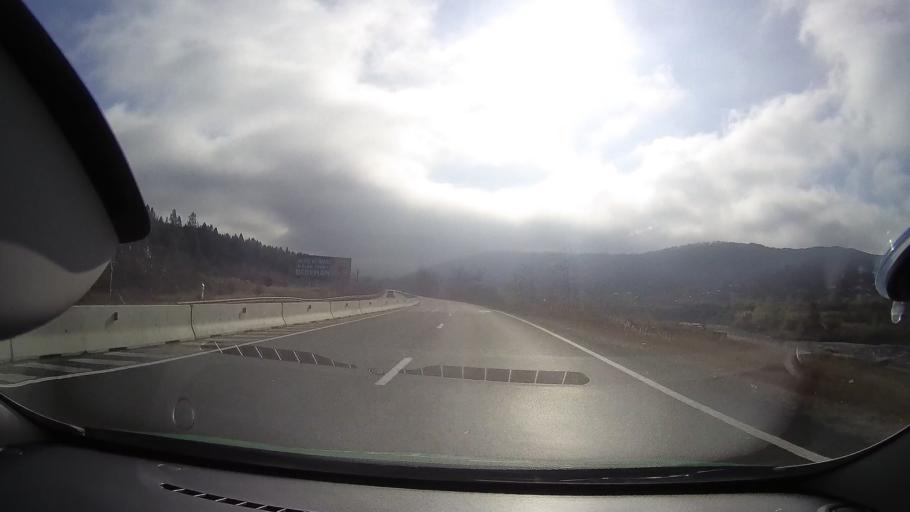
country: RO
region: Prahova
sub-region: Municipiul Campina
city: Campina
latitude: 45.1278
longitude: 25.7199
